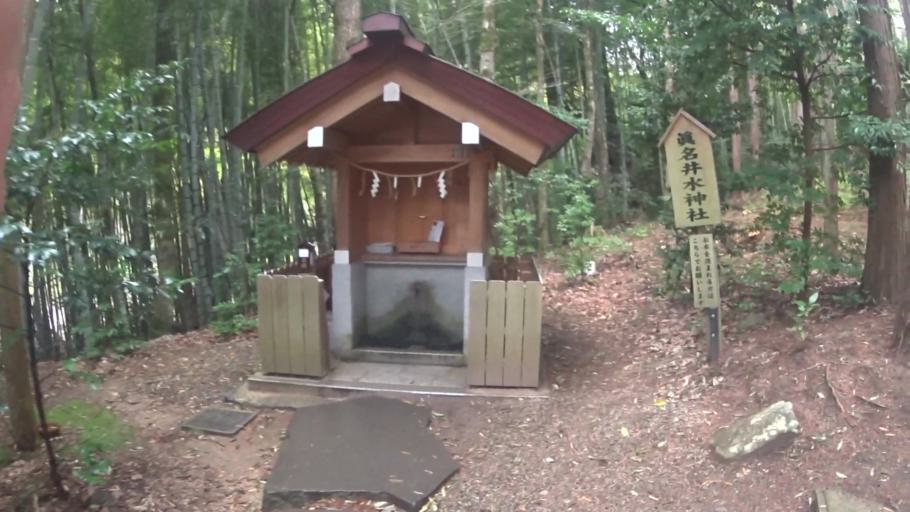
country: JP
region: Kyoto
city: Miyazu
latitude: 35.5861
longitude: 135.1985
